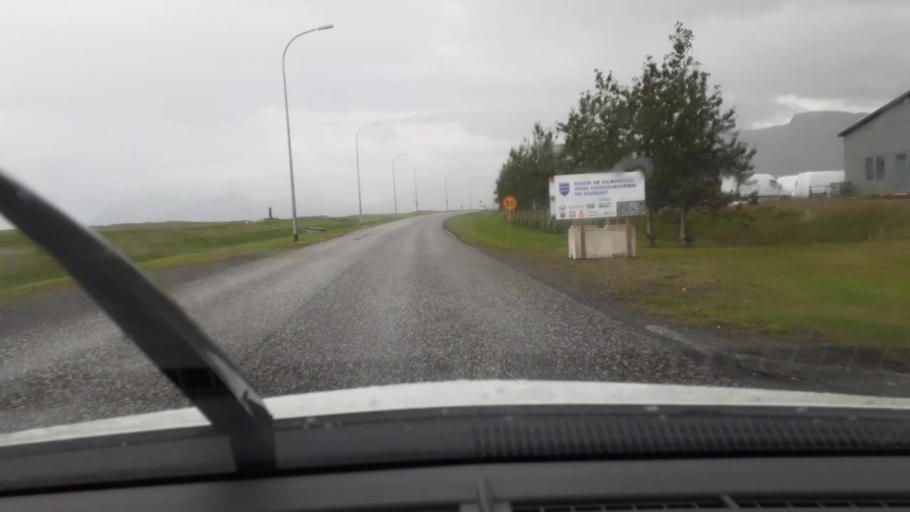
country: IS
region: West
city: Akranes
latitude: 64.3251
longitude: -22.0677
